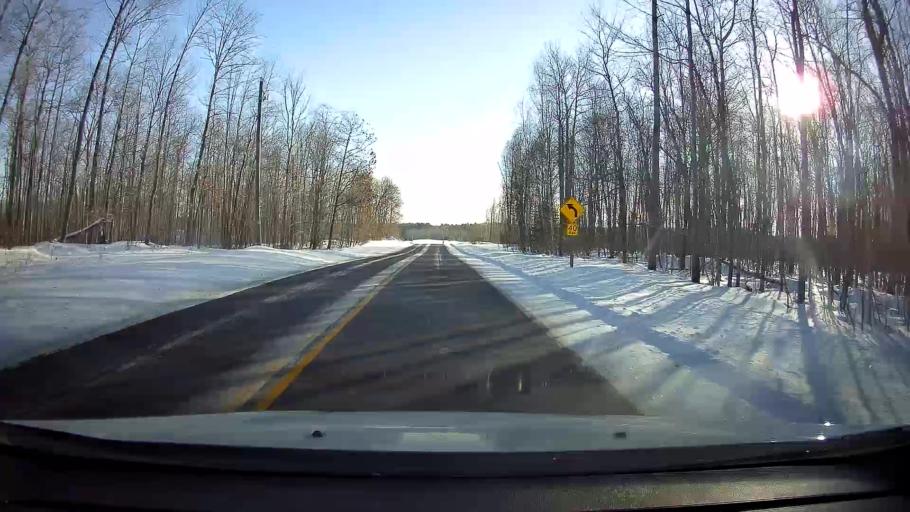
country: US
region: Wisconsin
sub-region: Sawyer County
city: Little Round Lake
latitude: 46.1141
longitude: -91.3255
